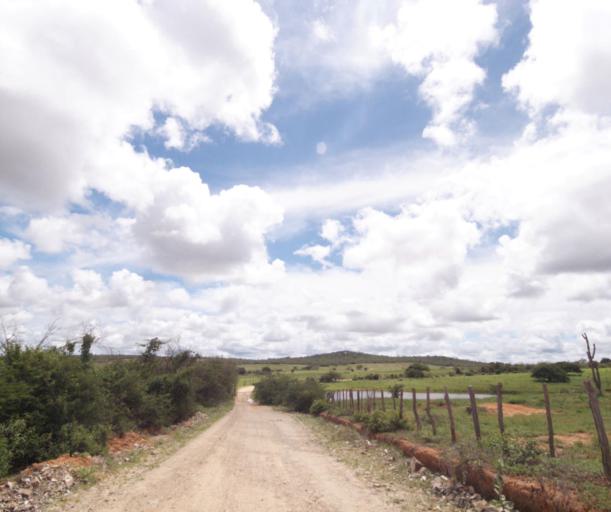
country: BR
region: Bahia
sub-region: Tanhacu
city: Tanhacu
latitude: -14.1749
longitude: -41.1323
